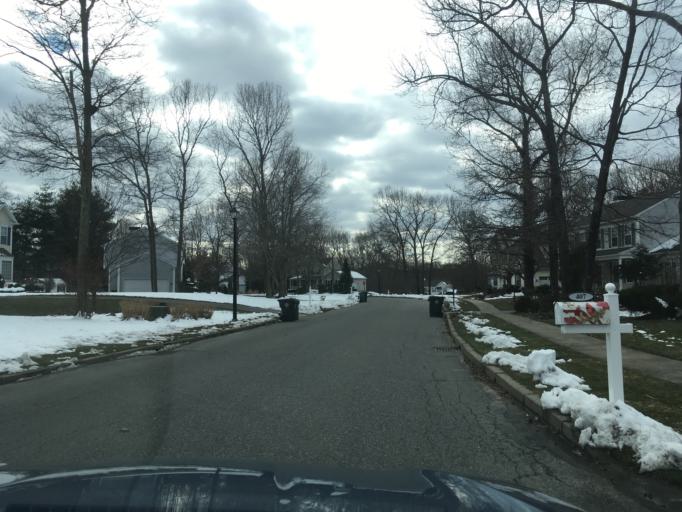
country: US
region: Rhode Island
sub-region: Kent County
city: East Greenwich
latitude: 41.6766
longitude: -71.4730
